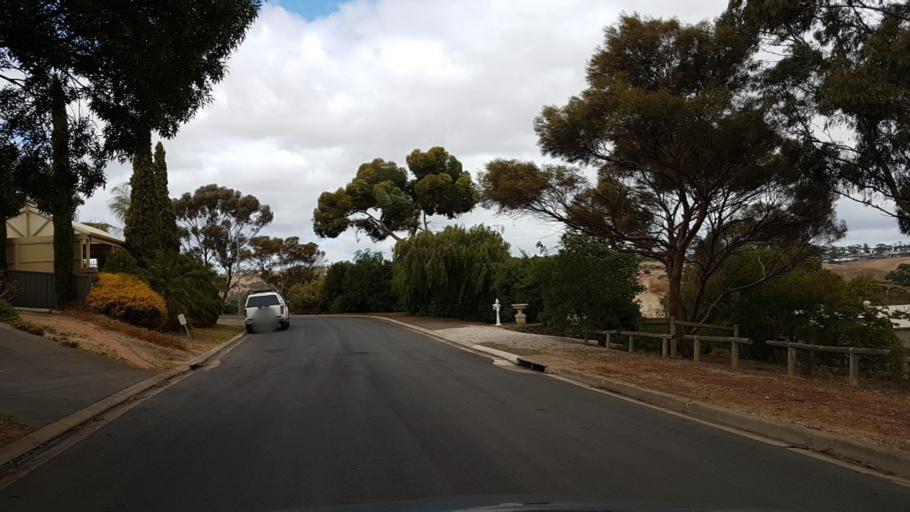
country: AU
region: South Australia
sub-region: Gawler
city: Gawler
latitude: -34.6076
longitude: 138.7584
